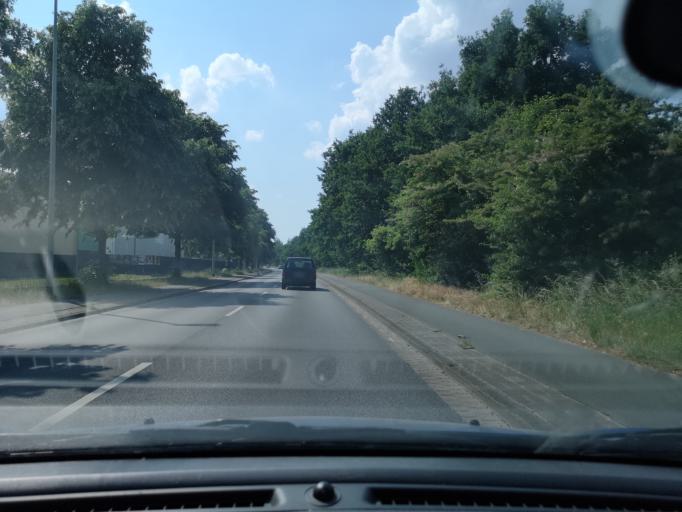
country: DE
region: Lower Saxony
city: Langenhagen
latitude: 52.4212
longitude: 9.7497
